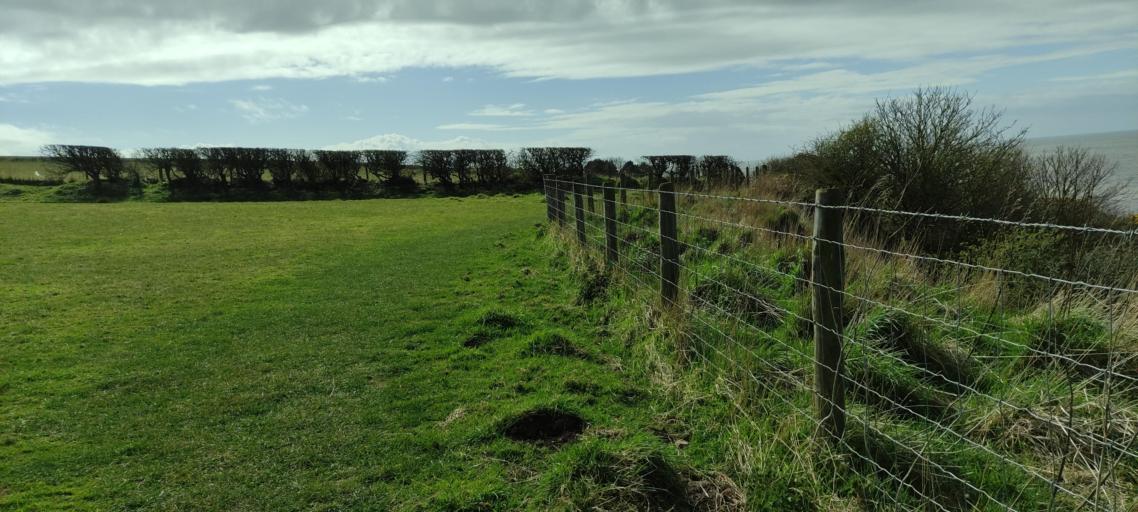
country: GB
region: England
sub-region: Cumbria
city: Maryport
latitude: 54.7249
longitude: -3.4911
